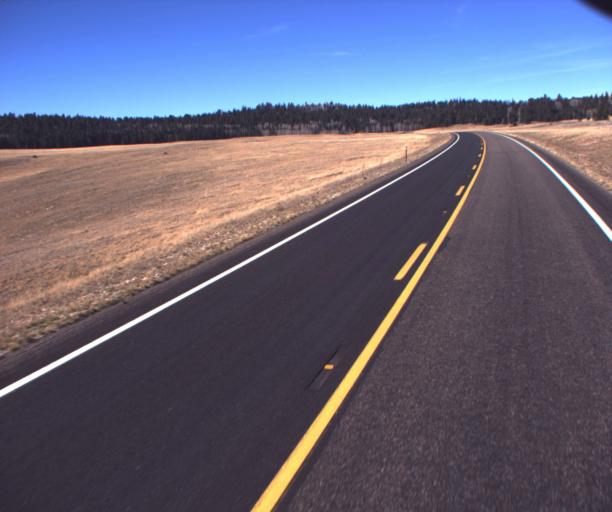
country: US
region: Arizona
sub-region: Coconino County
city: Grand Canyon
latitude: 36.4974
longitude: -112.1334
